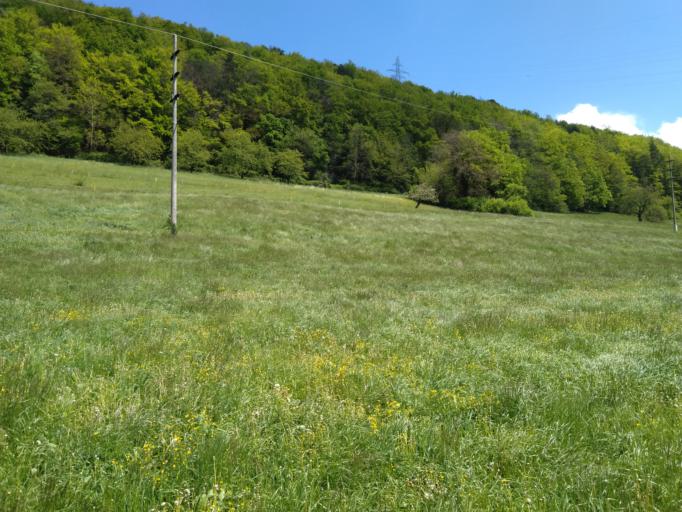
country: CH
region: Basel-Landschaft
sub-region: Bezirk Laufen
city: Wahlen
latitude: 47.3824
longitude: 7.4943
